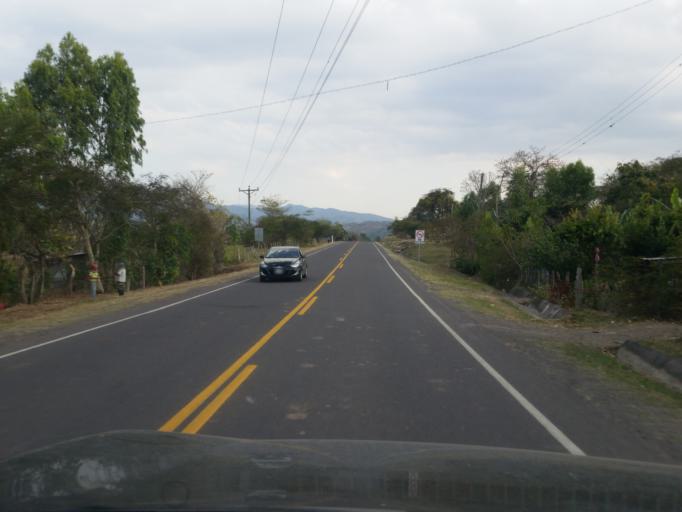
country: NI
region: Jinotega
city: San Rafael del Norte
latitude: 13.1644
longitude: -86.0635
